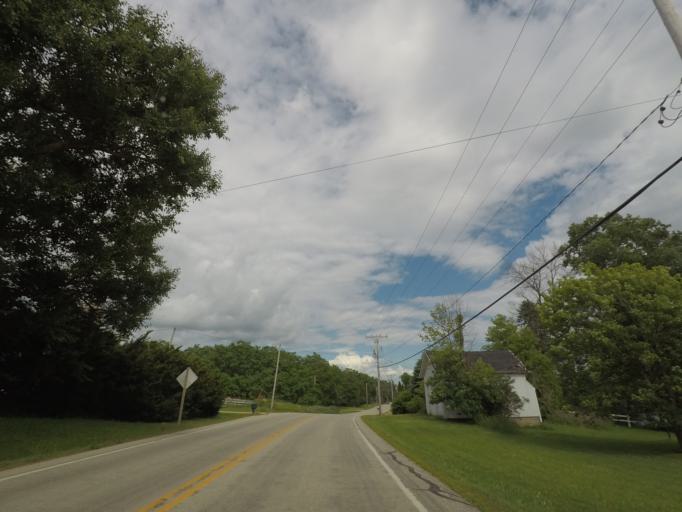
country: US
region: Wisconsin
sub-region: Dane County
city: Belleville
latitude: 42.8282
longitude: -89.5168
